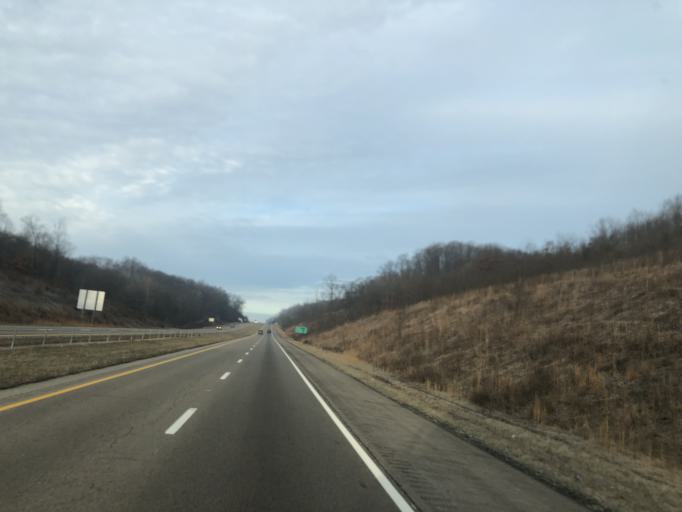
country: US
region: Ohio
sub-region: Athens County
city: Nelsonville
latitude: 39.4705
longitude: -82.2680
